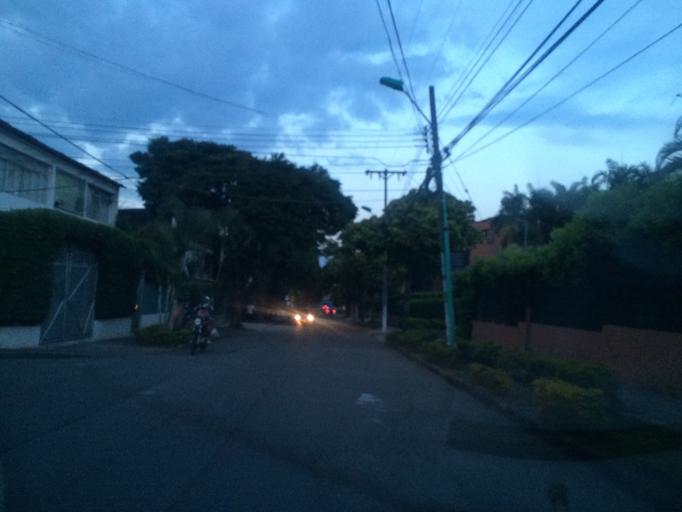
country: CO
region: Valle del Cauca
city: Cali
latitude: 3.4239
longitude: -76.5494
